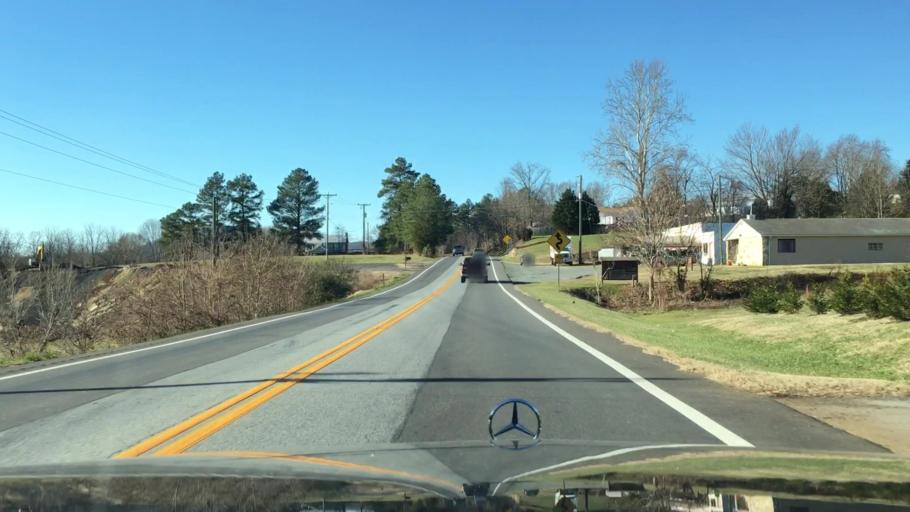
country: US
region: Virginia
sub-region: Botetourt County
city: Blue Ridge
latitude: 37.2701
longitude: -79.7644
